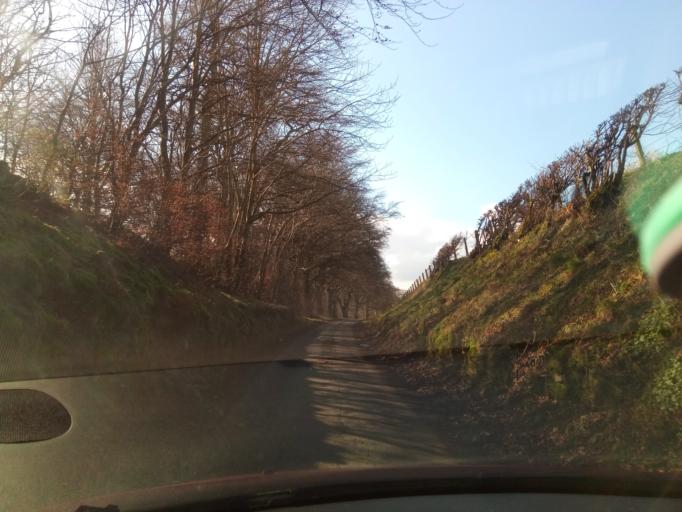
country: GB
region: Scotland
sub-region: The Scottish Borders
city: Hawick
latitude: 55.4201
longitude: -2.8103
